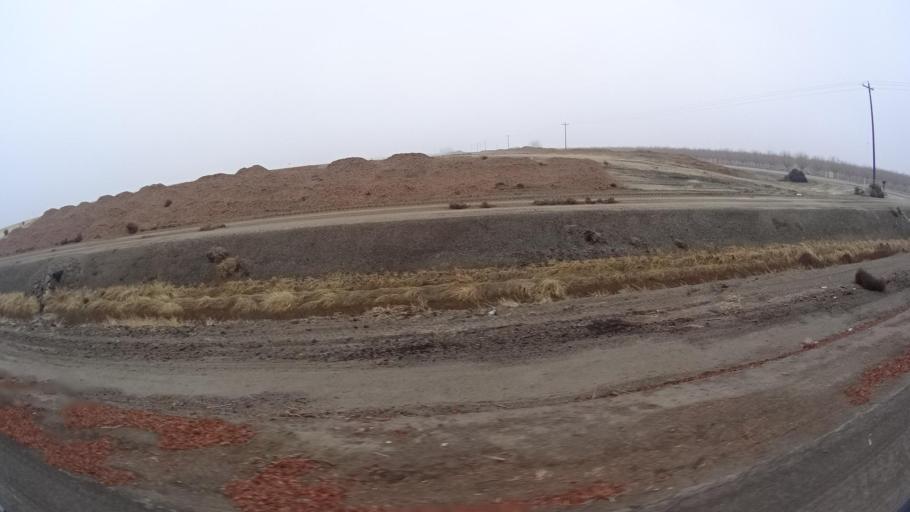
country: US
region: California
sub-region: Kern County
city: Buttonwillow
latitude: 35.4123
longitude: -119.5179
